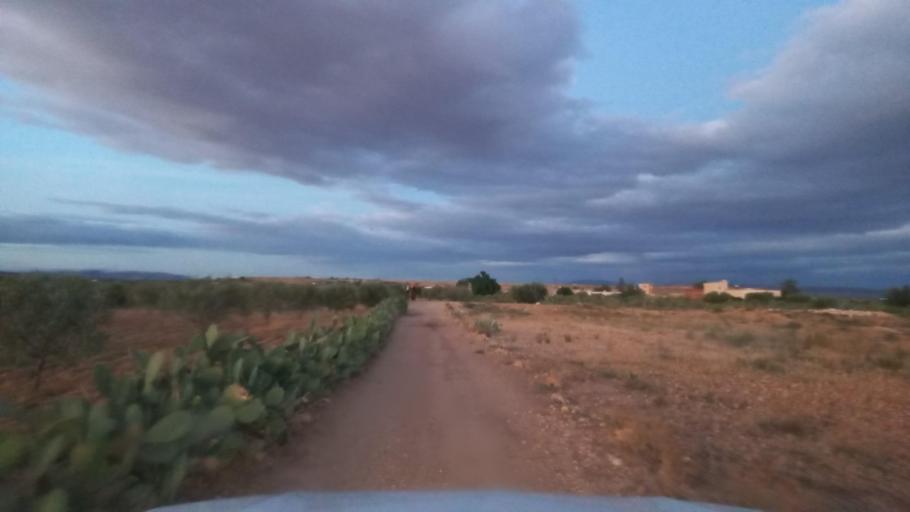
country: TN
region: Al Qasrayn
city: Kasserine
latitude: 35.2586
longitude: 8.9399
